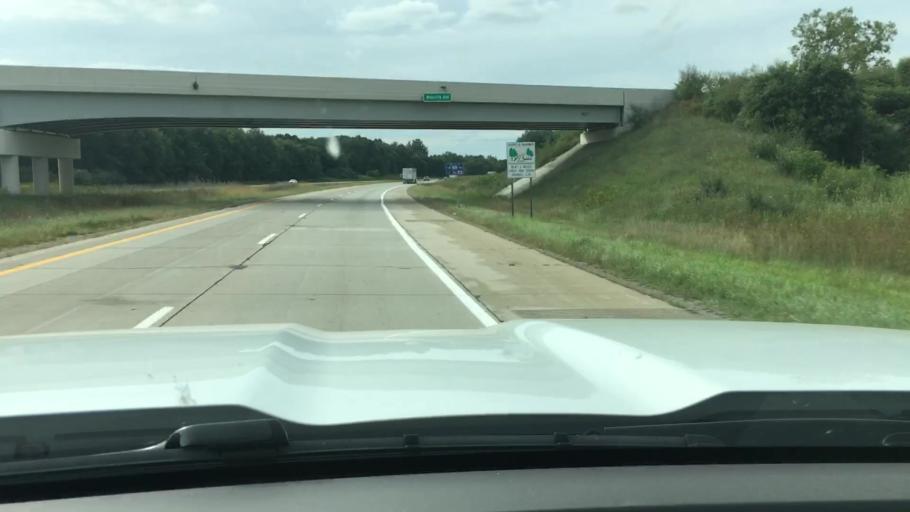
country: US
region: Michigan
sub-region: Lapeer County
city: Lapeer
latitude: 43.0129
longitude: -83.2819
